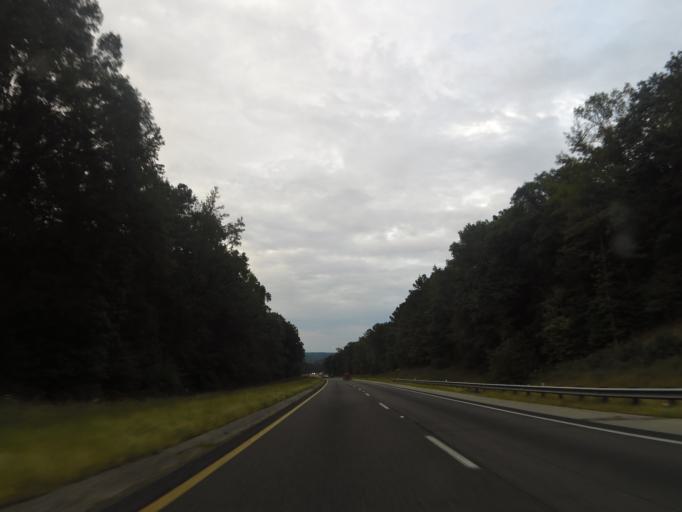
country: US
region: Alabama
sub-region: Saint Clair County
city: Springville
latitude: 33.7360
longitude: -86.4909
